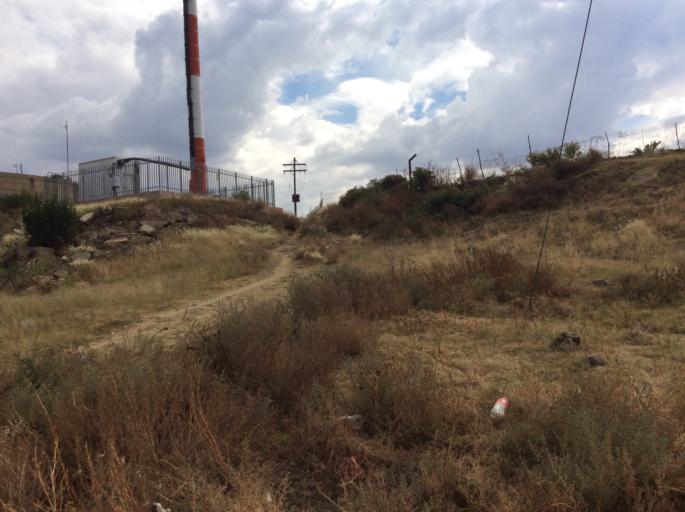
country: LS
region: Mafeteng
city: Mafeteng
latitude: -29.7235
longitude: 27.0319
